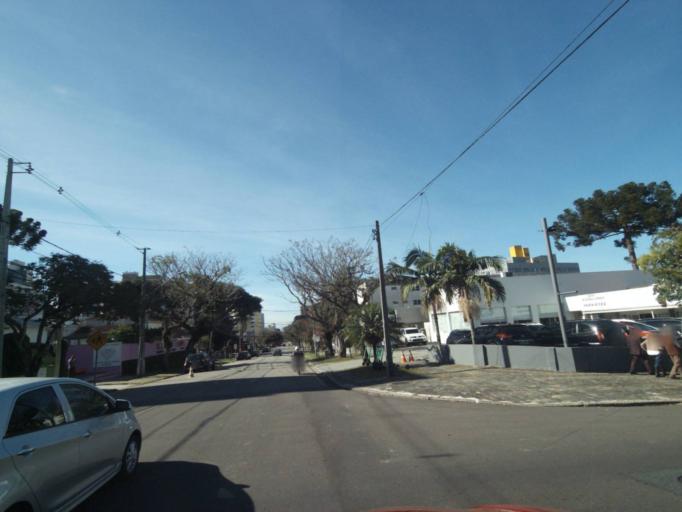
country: BR
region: Parana
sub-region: Curitiba
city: Curitiba
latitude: -25.4343
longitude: -49.2939
